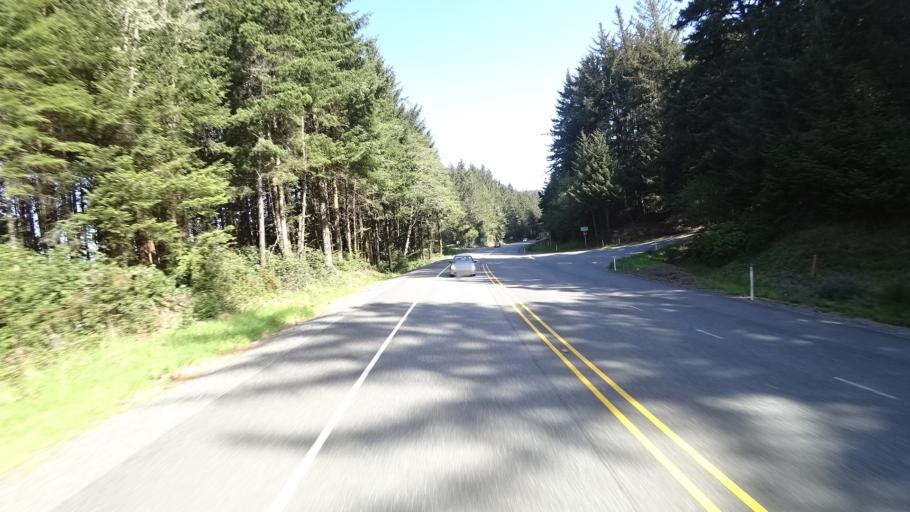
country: US
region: Oregon
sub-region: Curry County
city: Brookings
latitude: 42.1399
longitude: -124.3523
